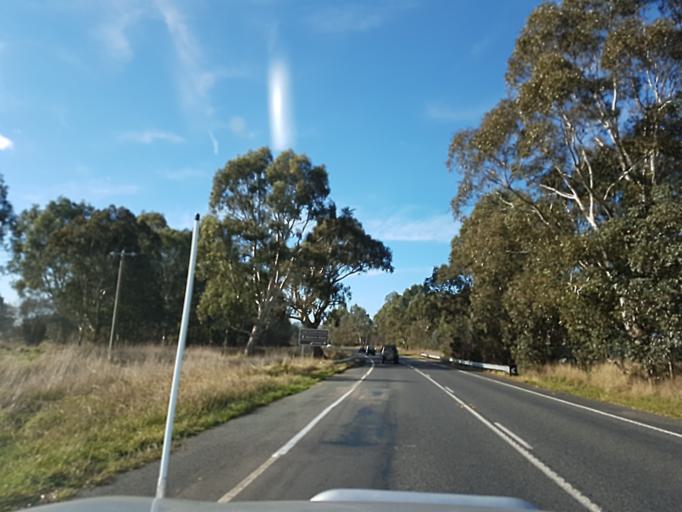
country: AU
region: Victoria
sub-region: Murrindindi
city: Alexandra
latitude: -37.1518
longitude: 145.5792
